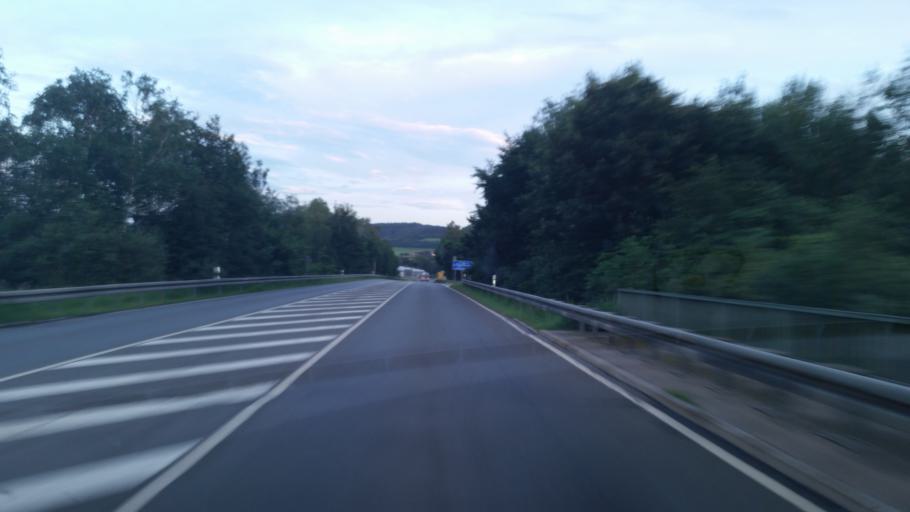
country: DE
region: Bavaria
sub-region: Upper Palatinate
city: Luhe-Wildenau
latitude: 49.5929
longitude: 12.1412
